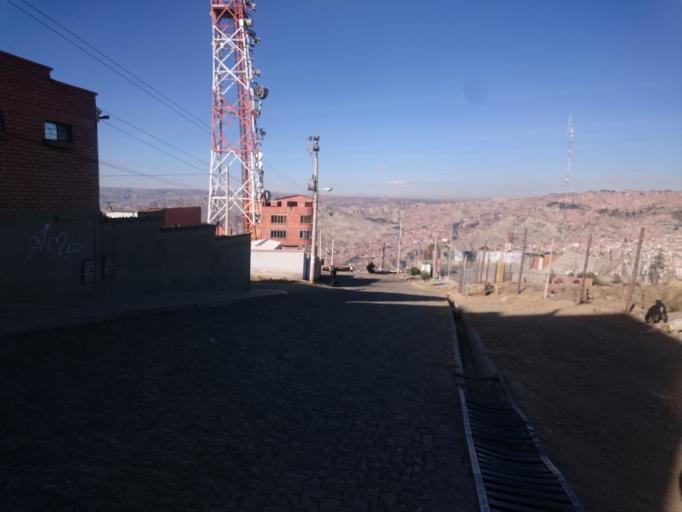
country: BO
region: La Paz
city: La Paz
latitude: -16.4897
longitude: -68.1067
